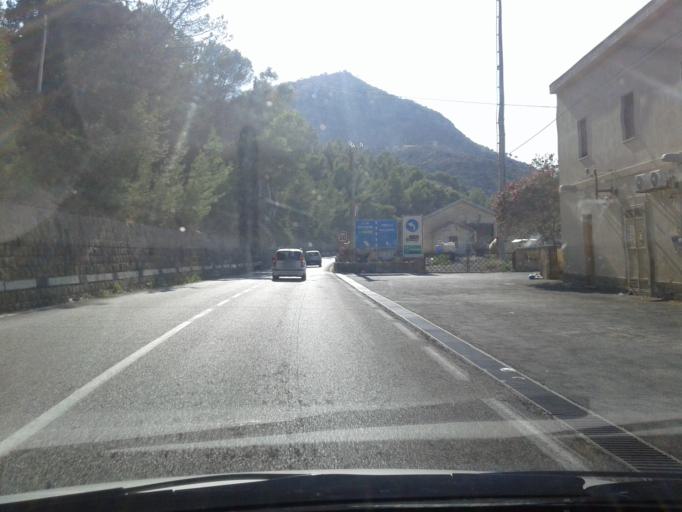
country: IT
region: Sicily
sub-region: Palermo
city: Pollina
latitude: 38.0144
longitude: 14.1090
